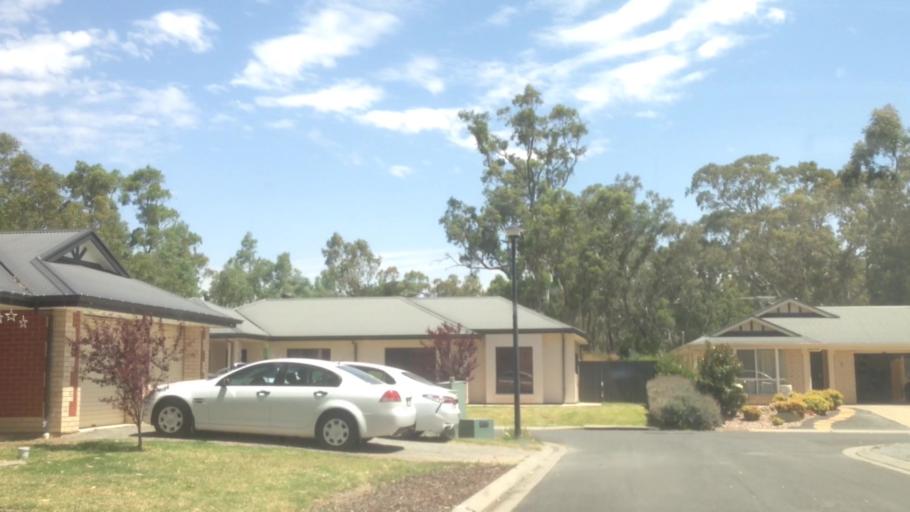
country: AU
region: South Australia
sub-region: Adelaide Hills
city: Birdwood
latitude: -34.8176
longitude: 138.9705
